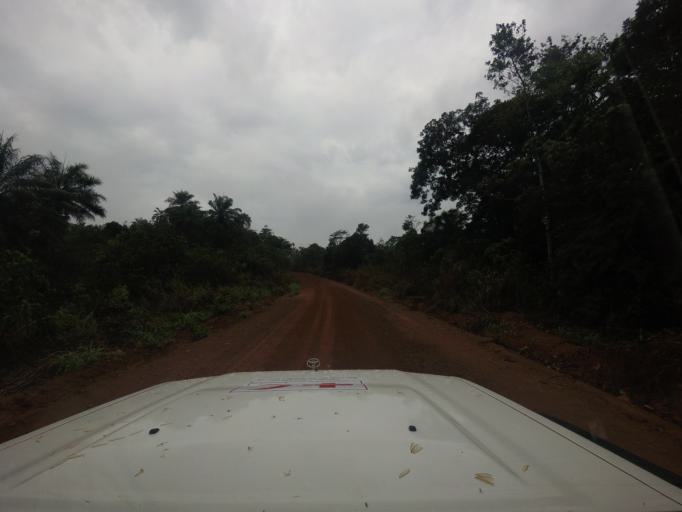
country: LR
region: Lofa
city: Voinjama
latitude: 8.3827
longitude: -9.8358
